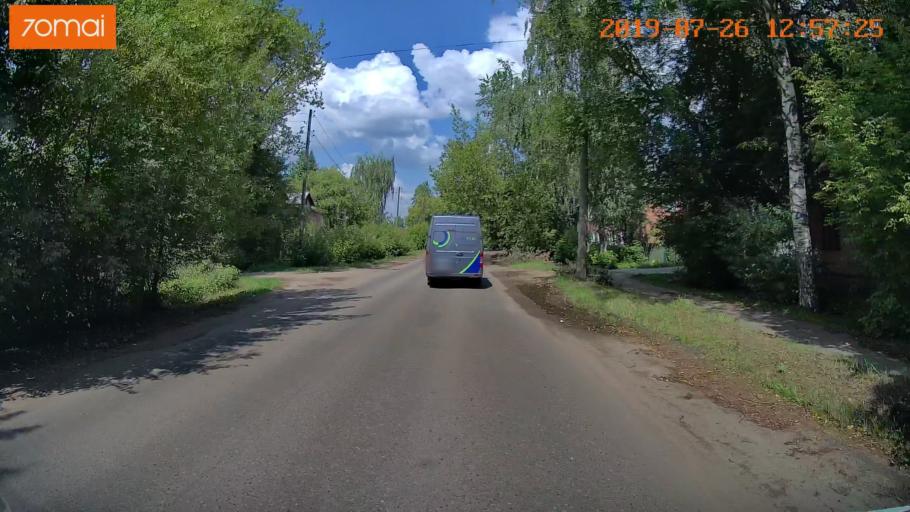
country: RU
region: Ivanovo
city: Bogorodskoye
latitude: 57.0190
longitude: 41.0208
